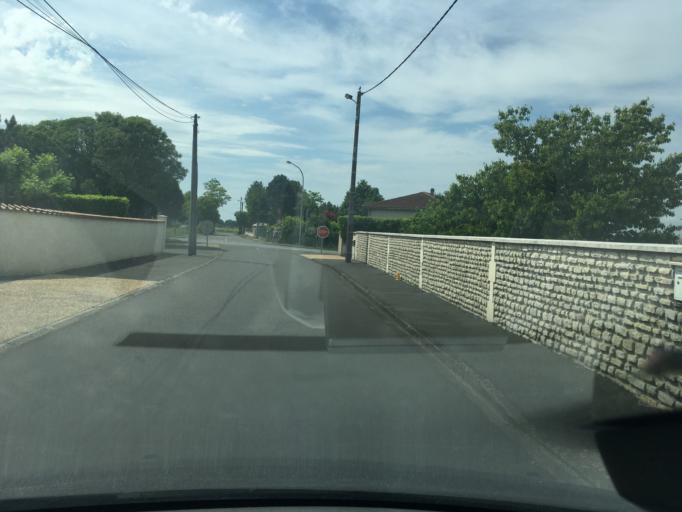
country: FR
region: Poitou-Charentes
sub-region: Departement de la Charente
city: Chateaubernard
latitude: 45.6754
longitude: -0.3300
